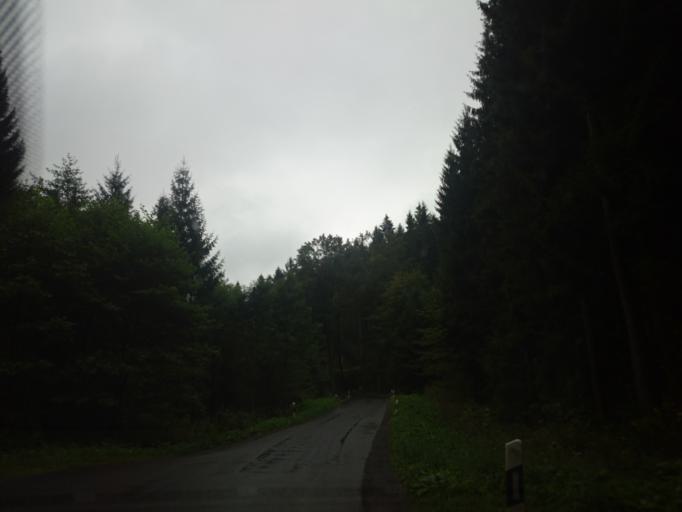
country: DE
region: Saxony
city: Leubsdorf
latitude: 50.8172
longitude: 13.1912
